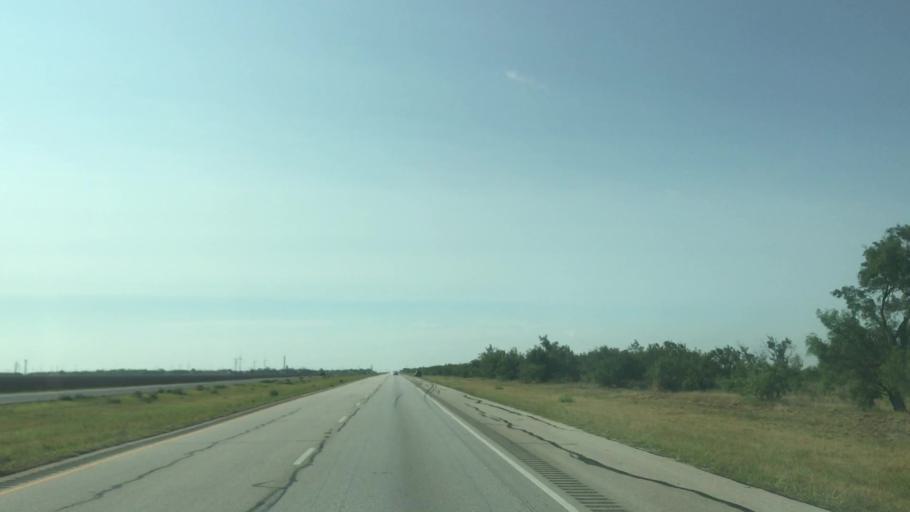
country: US
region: Texas
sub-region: Scurry County
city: Snyder
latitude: 32.6511
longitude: -100.7765
